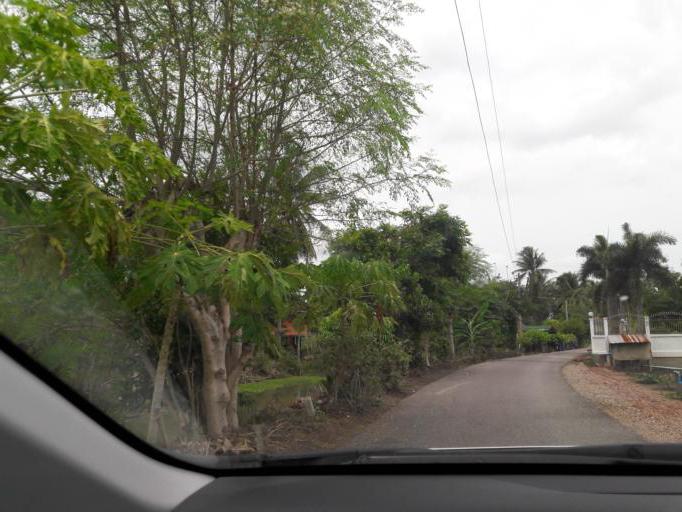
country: TH
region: Samut Sakhon
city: Ban Phaeo
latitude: 13.5954
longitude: 100.0273
